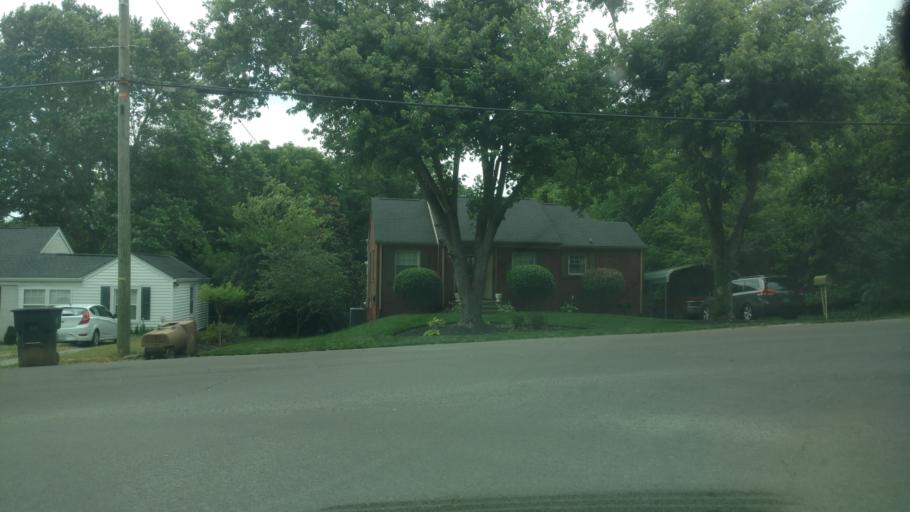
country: US
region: Tennessee
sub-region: Davidson County
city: Lakewood
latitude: 36.2089
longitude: -86.7102
